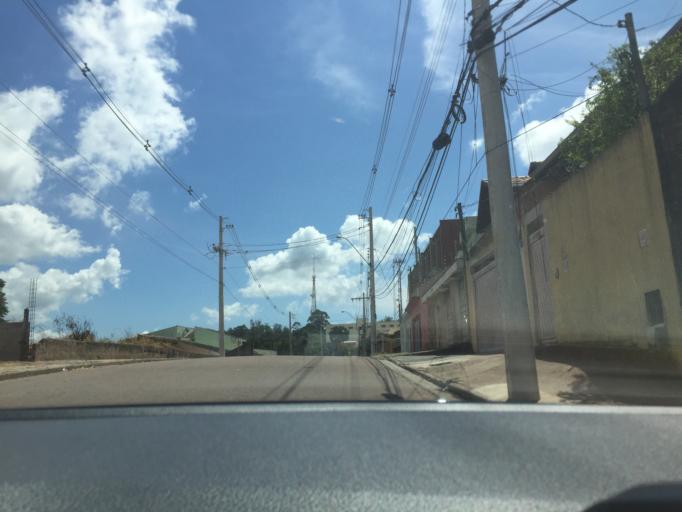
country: BR
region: Sao Paulo
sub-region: Jundiai
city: Jundiai
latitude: -23.1760
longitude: -46.8707
